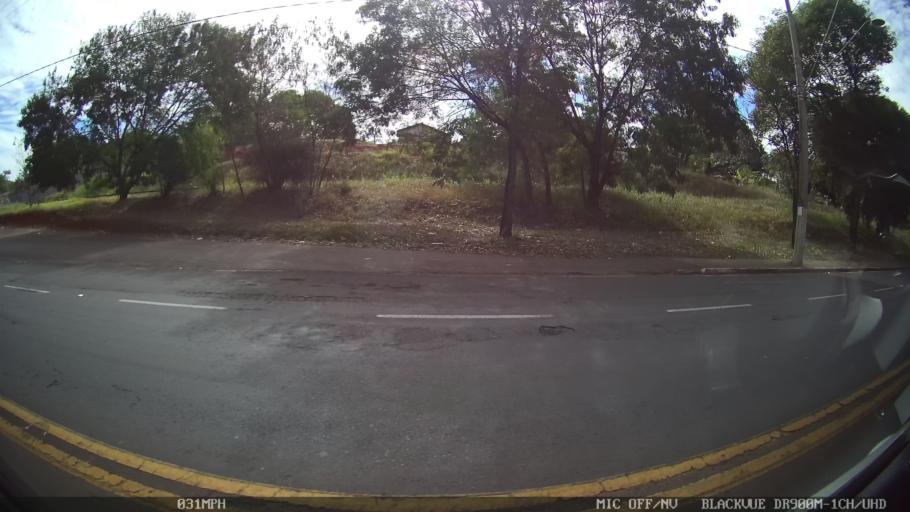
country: BR
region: Sao Paulo
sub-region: Catanduva
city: Catanduva
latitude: -21.1385
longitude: -48.9641
